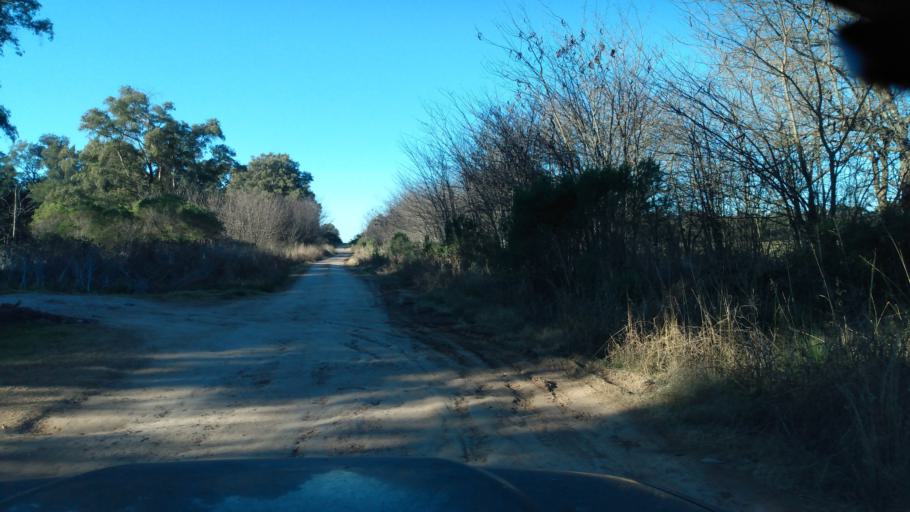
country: AR
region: Buenos Aires
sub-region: Partido de Lujan
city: Lujan
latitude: -34.5581
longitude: -59.1562
